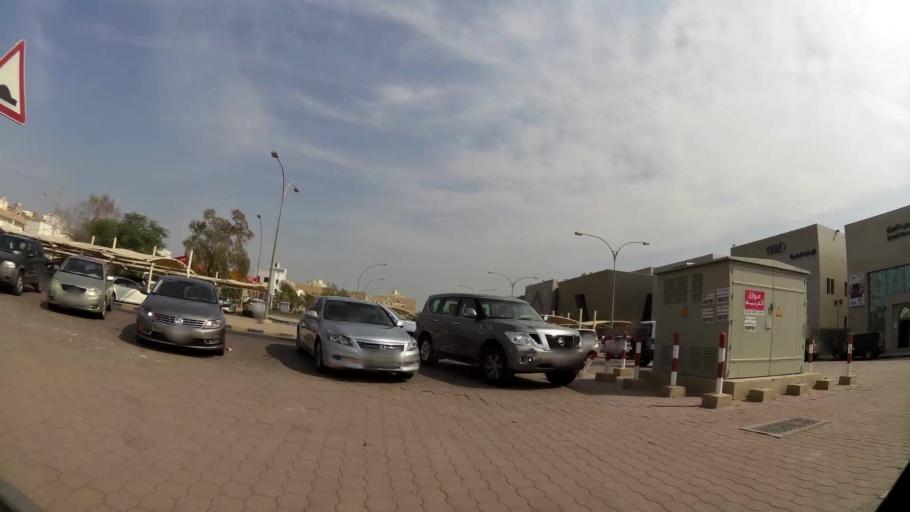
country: KW
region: Al Asimah
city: Ash Shamiyah
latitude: 29.3401
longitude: 47.9618
